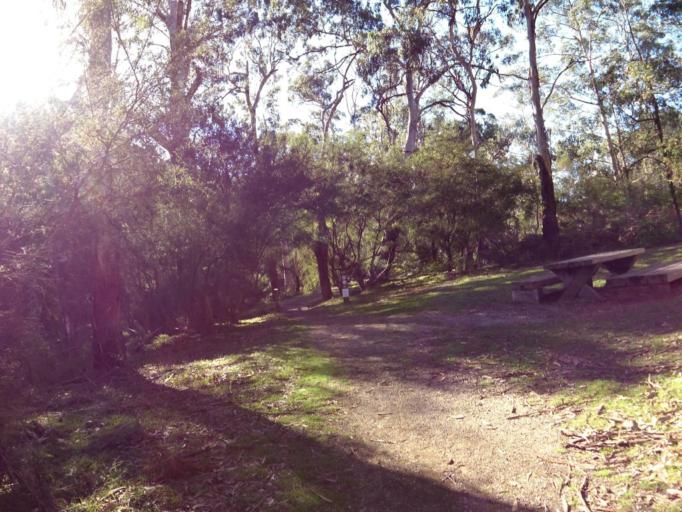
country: AU
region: Victoria
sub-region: Nillumbik
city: North Warrandyte
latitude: -37.7349
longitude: 145.1985
